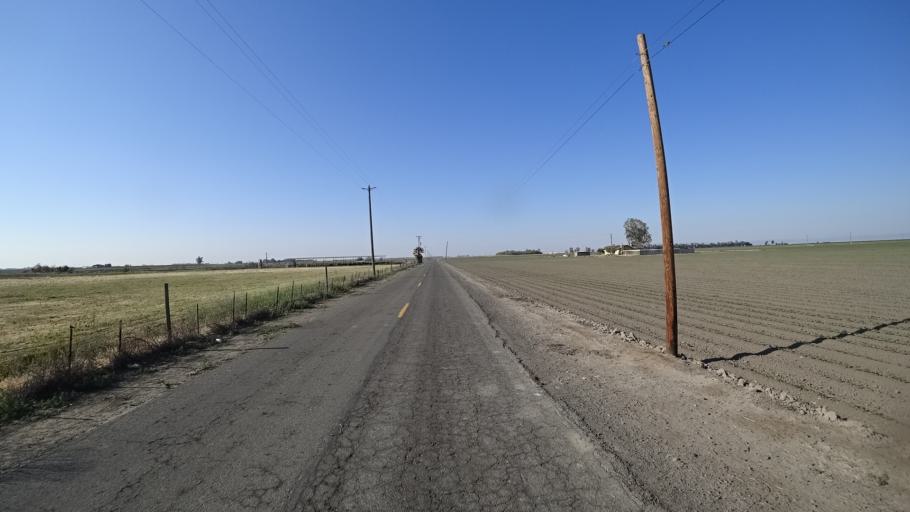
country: US
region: California
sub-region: Fresno County
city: Riverdale
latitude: 36.3892
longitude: -119.9277
